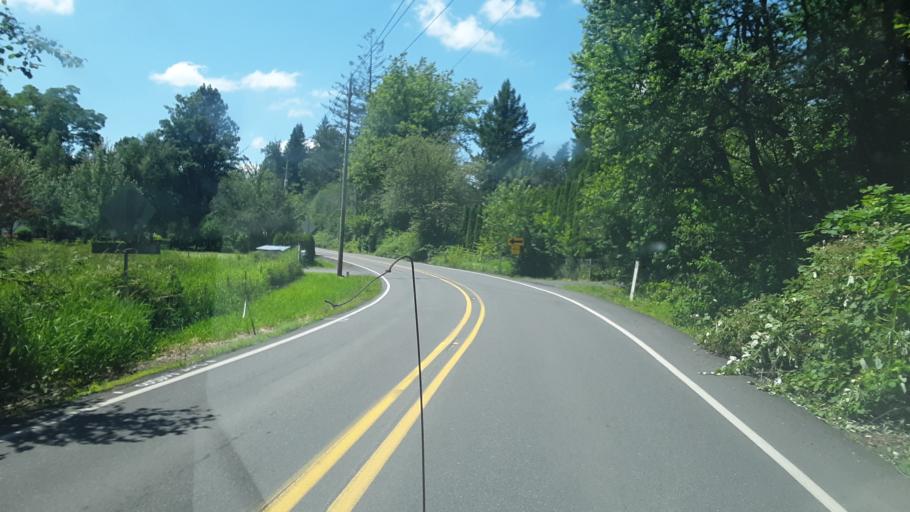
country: US
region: Washington
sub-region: Clark County
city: Amboy
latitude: 45.8956
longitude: -122.4534
